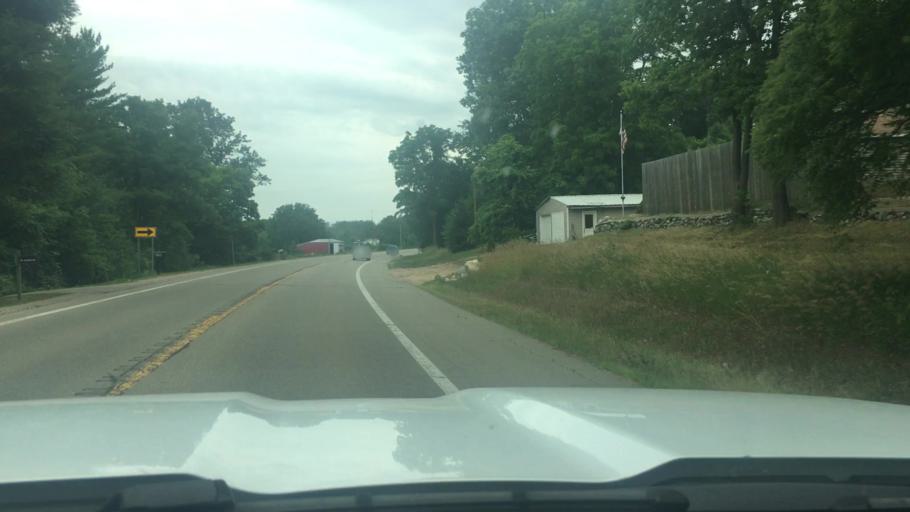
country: US
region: Michigan
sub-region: Ionia County
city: Saranac
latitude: 42.9523
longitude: -85.1779
